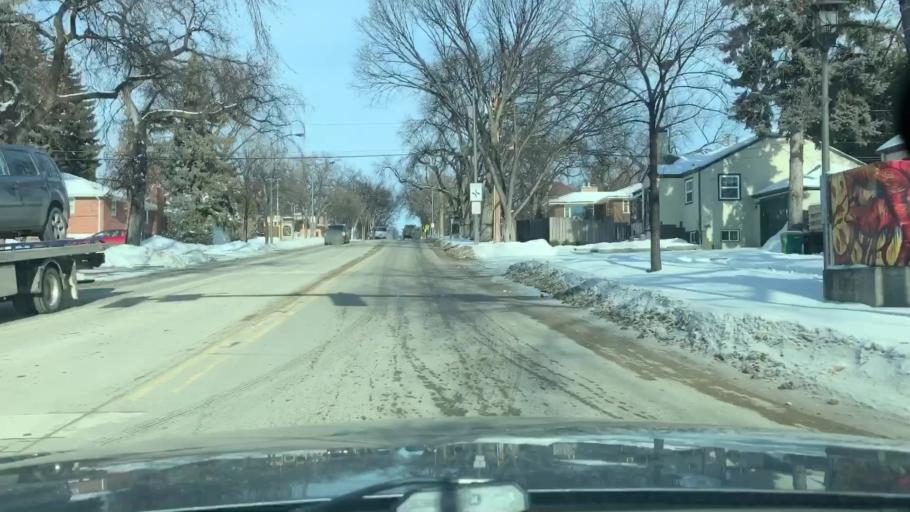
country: US
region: North Dakota
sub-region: Burleigh County
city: Bismarck
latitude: 46.8088
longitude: -100.7943
